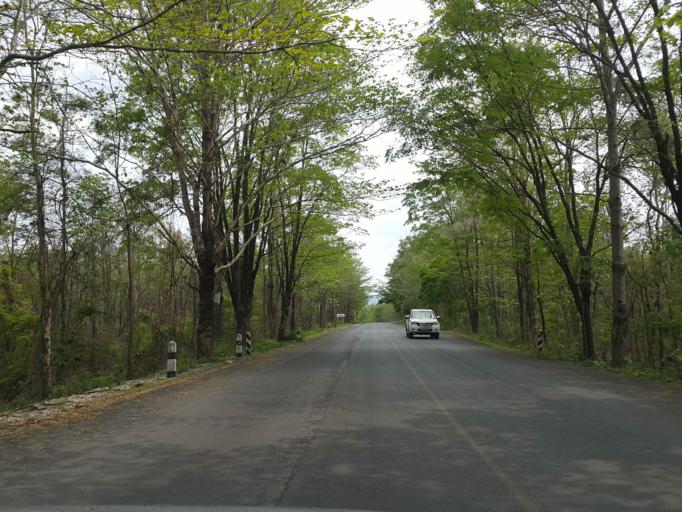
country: TH
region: Sukhothai
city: Thung Saliam
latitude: 17.4438
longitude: 99.3720
